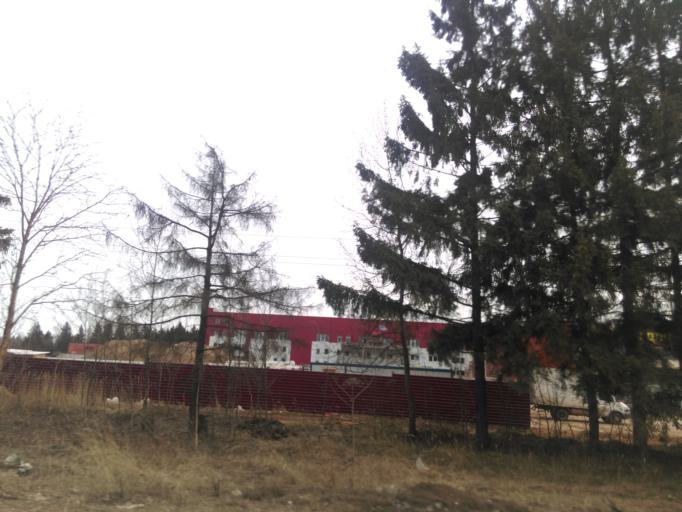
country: RU
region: Moskovskaya
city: Tuchkovo
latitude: 55.6070
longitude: 36.4933
